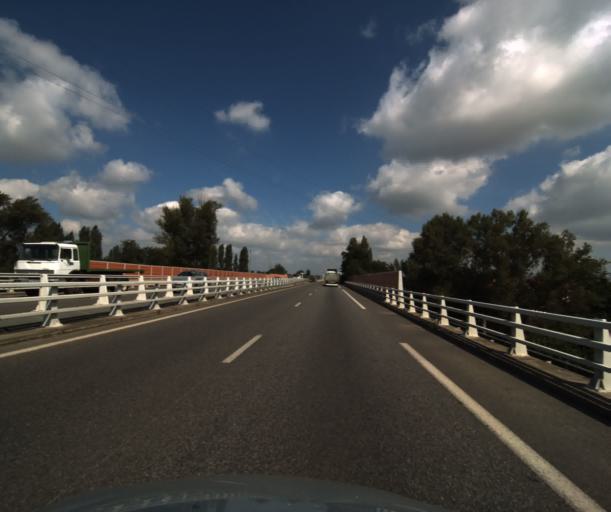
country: FR
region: Midi-Pyrenees
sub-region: Departement de la Haute-Garonne
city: Pinsaguel
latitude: 43.5105
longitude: 1.3823
